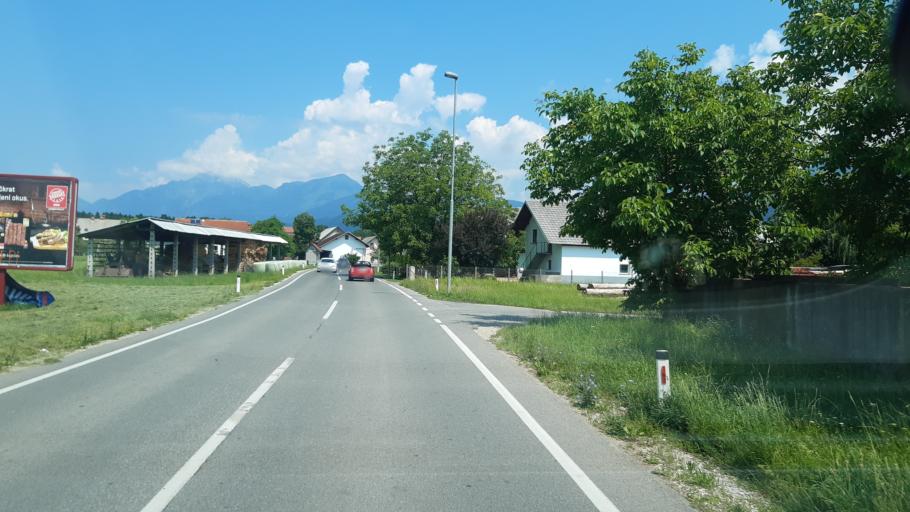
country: SI
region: Cerklje na Gorenjskem
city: Cerklje na Gorenjskem
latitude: 46.2368
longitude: 14.4852
